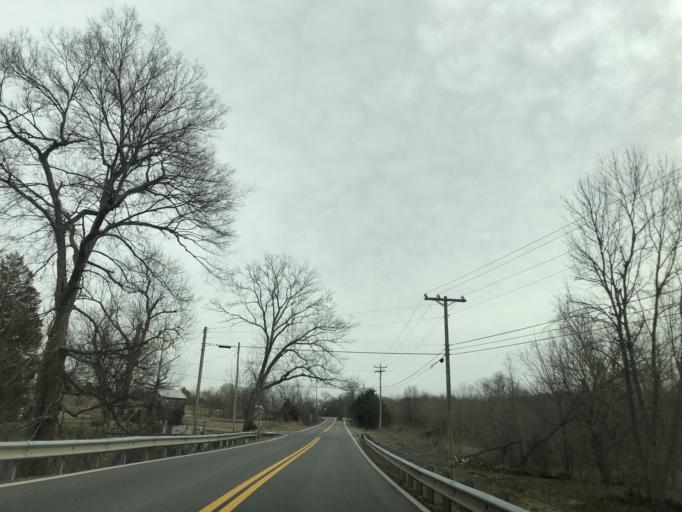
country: US
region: Tennessee
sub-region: Robertson County
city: Greenbrier
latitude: 36.4840
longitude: -86.7911
